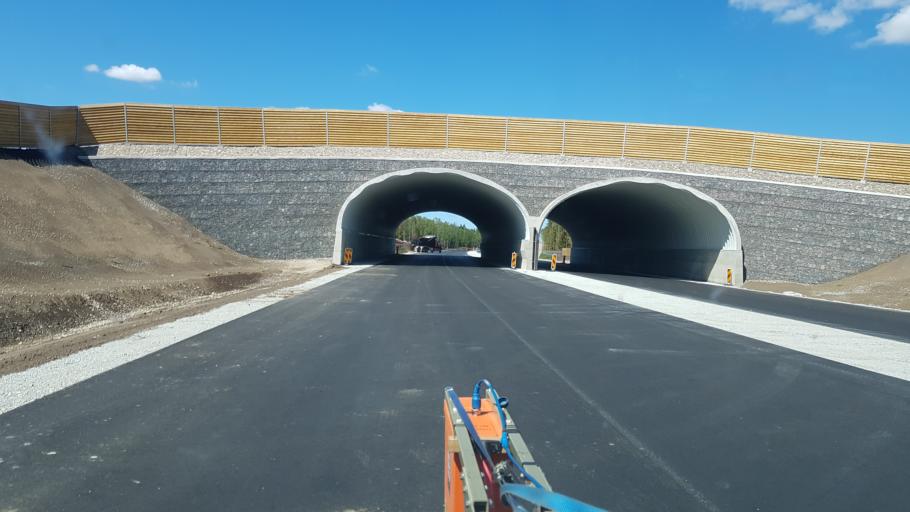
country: EE
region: Harju
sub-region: Anija vald
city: Kehra
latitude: 59.1219
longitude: 25.2793
